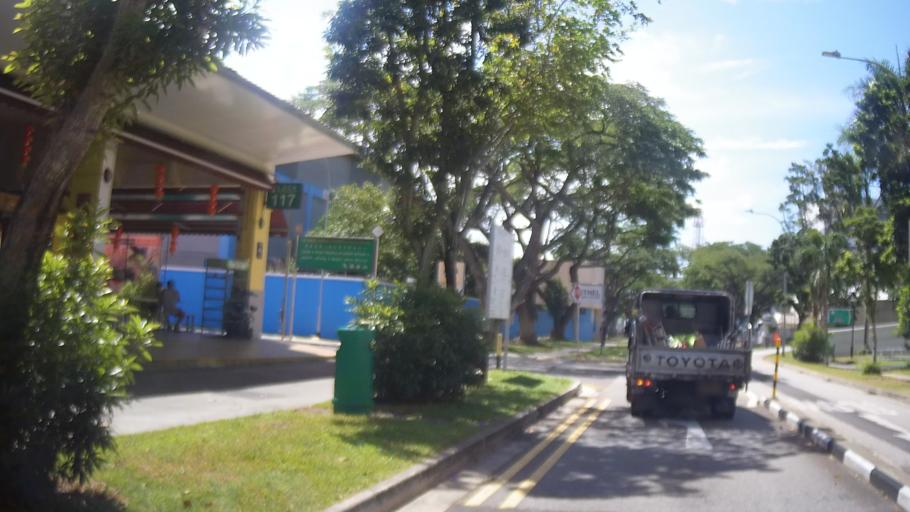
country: SG
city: Singapore
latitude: 1.3208
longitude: 103.8870
